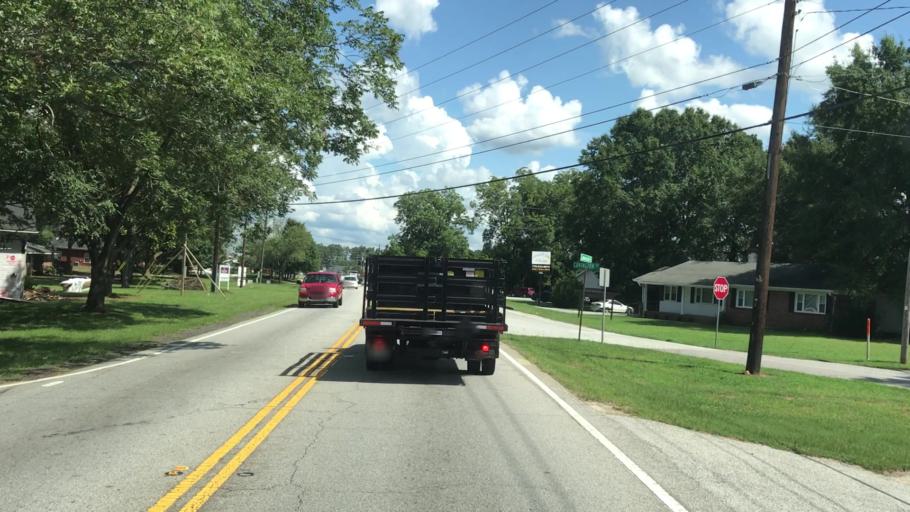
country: US
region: Georgia
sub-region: Walton County
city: Loganville
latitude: 33.8368
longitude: -83.8916
